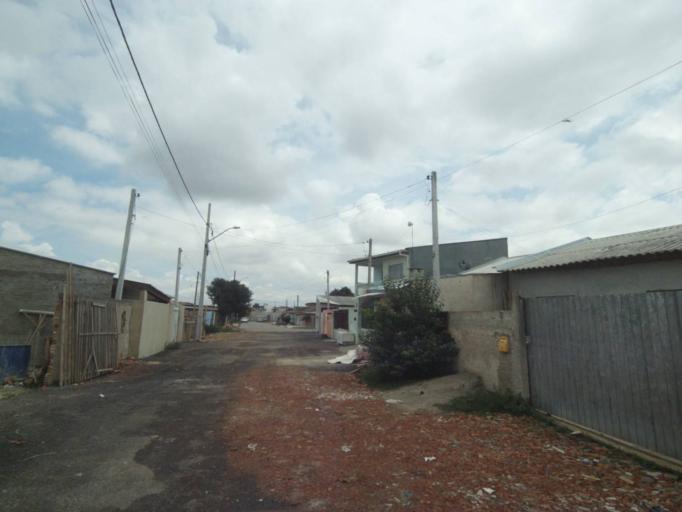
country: BR
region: Parana
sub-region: Pinhais
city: Pinhais
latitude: -25.4639
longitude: -49.1916
